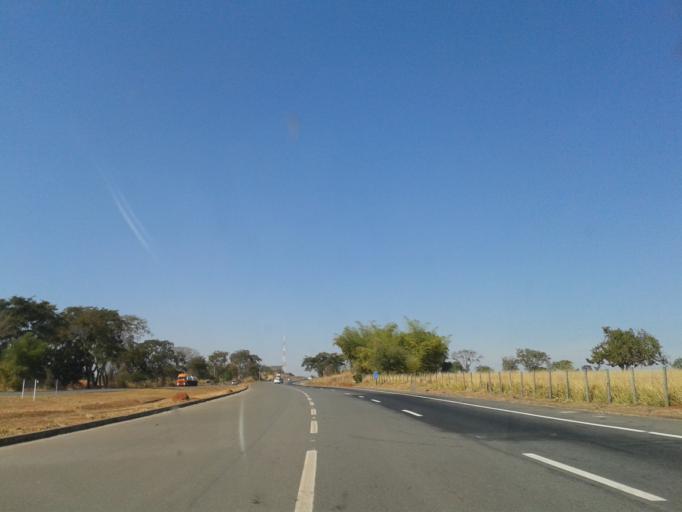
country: BR
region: Goias
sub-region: Piracanjuba
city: Piracanjuba
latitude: -17.2850
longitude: -49.2361
